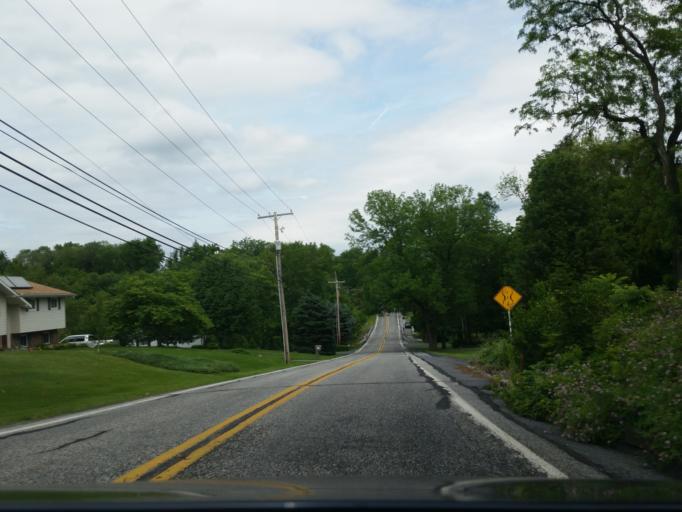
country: US
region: Pennsylvania
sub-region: Lebanon County
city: Palmyra
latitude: 40.3894
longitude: -76.6236
